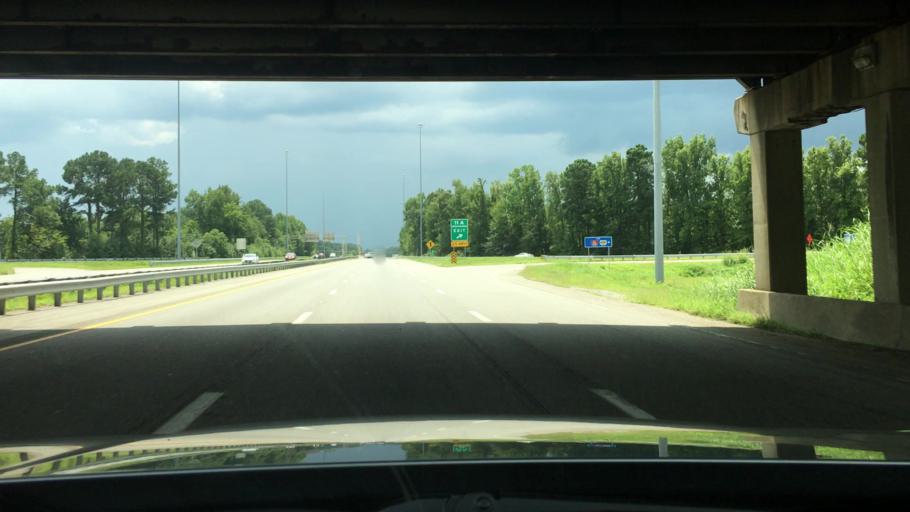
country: US
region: Virginia
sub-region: City of Emporia
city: Emporia
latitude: 36.7027
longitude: -77.5495
